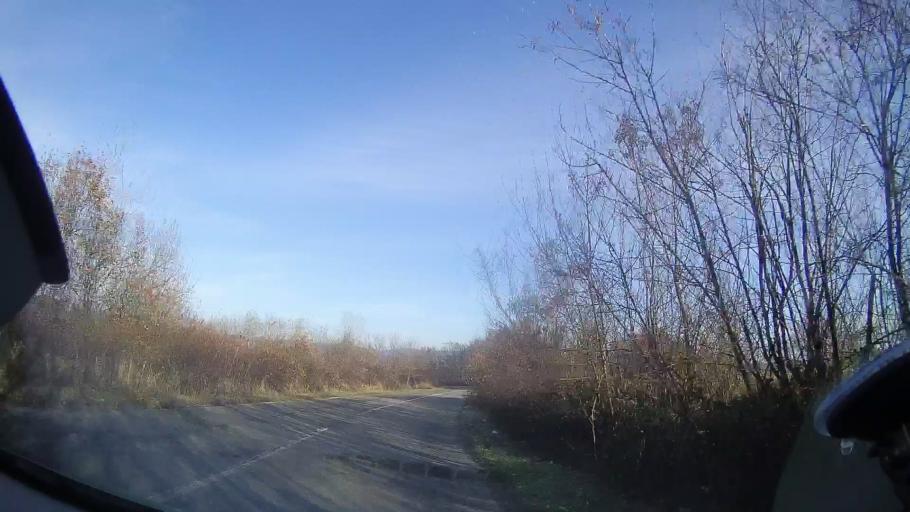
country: RO
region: Bihor
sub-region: Comuna Brusturi
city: Brusturi
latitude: 47.1097
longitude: 22.2588
